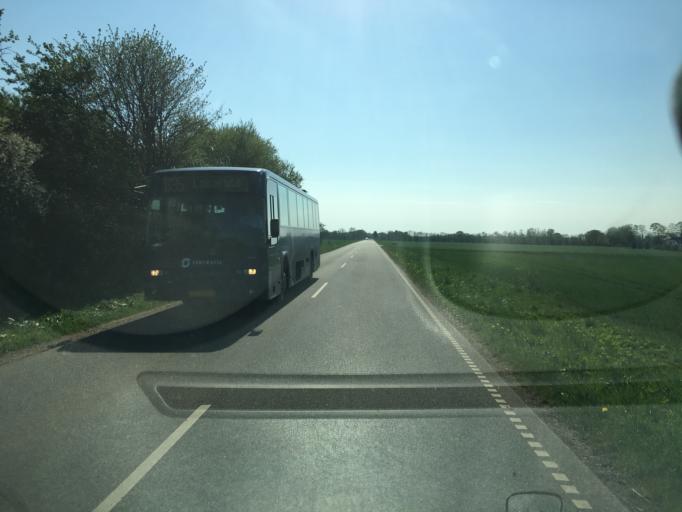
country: DK
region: South Denmark
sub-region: Haderslev Kommune
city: Vojens
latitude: 55.3049
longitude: 9.2669
